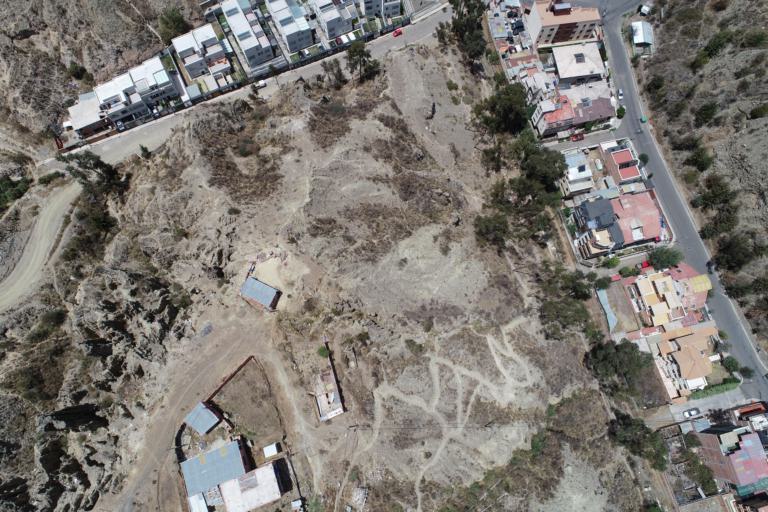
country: BO
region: La Paz
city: La Paz
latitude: -16.5216
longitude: -68.0789
